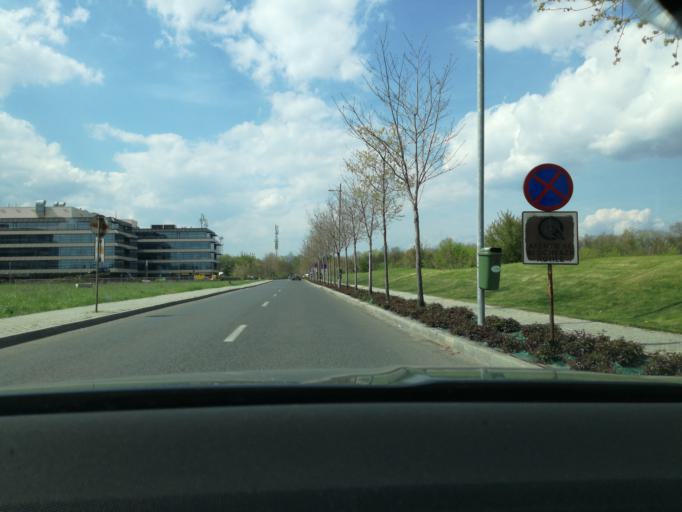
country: RO
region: Ilfov
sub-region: Comuna Otopeni
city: Otopeni
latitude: 44.5151
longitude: 26.0834
